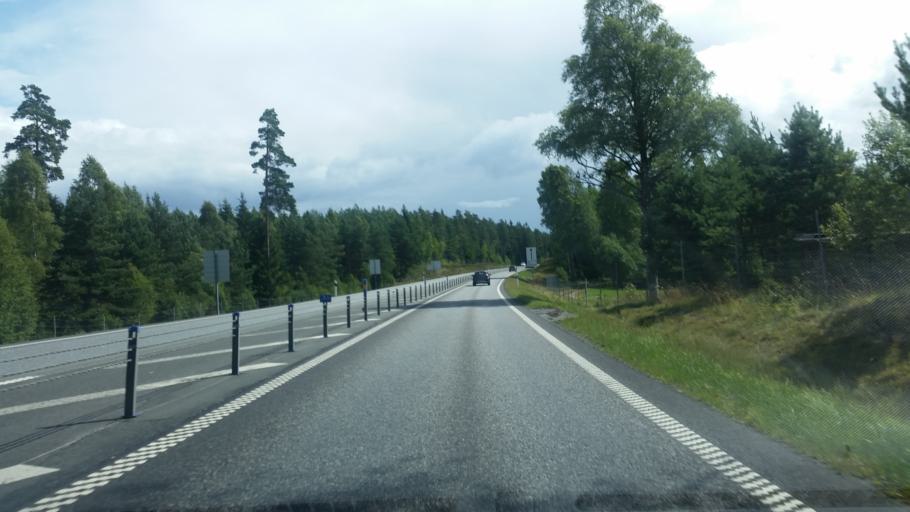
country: SE
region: Joenkoeping
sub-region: Mullsjo Kommun
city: Mullsjoe
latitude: 57.7692
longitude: 13.8018
